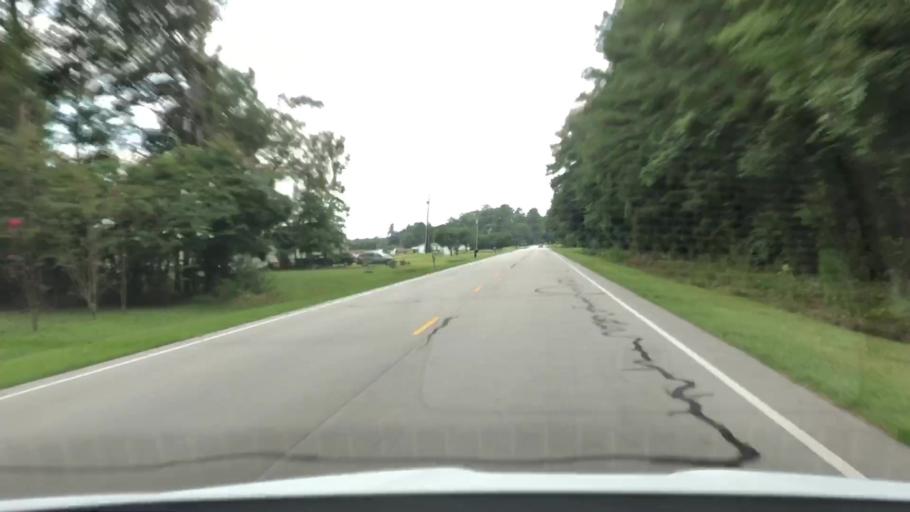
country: US
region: North Carolina
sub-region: Lenoir County
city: Kinston
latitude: 35.1170
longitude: -77.5130
